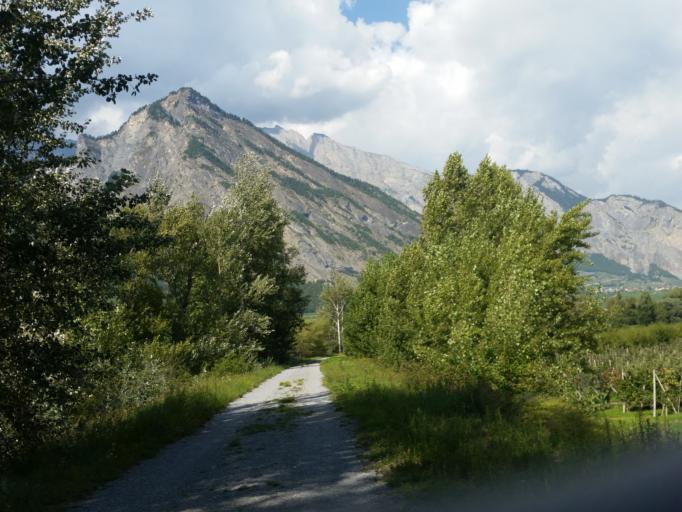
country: CH
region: Valais
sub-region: Martigny District
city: Leytron
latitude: 46.1724
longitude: 7.2010
